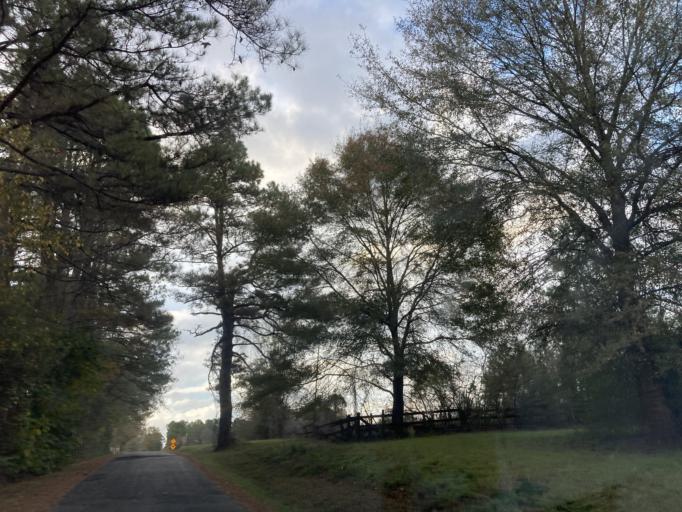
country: US
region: Mississippi
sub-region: Marion County
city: Columbia
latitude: 31.1935
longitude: -89.6454
